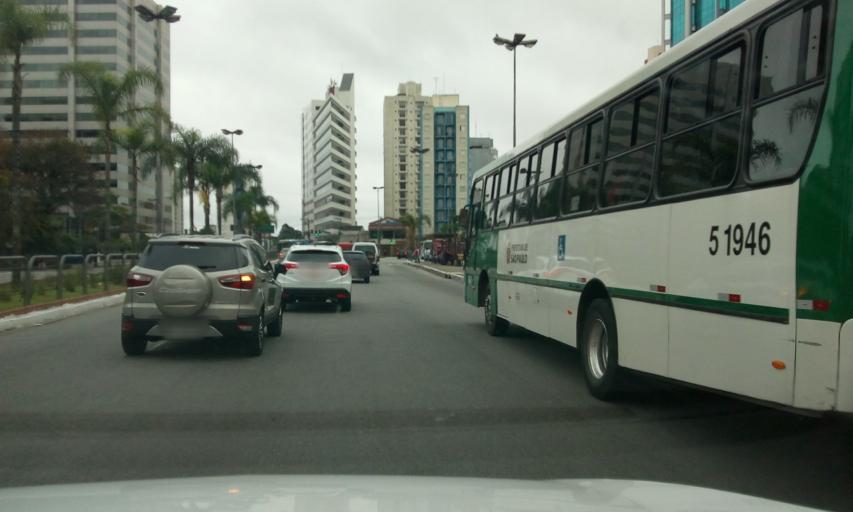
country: BR
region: Sao Paulo
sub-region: Diadema
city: Diadema
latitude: -23.6358
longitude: -46.6412
